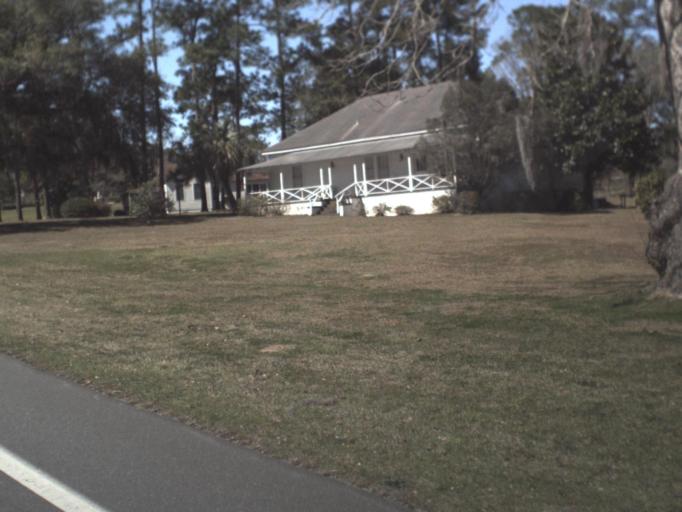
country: US
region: Florida
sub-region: Gadsden County
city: Chattahoochee
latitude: 30.7015
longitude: -84.8358
